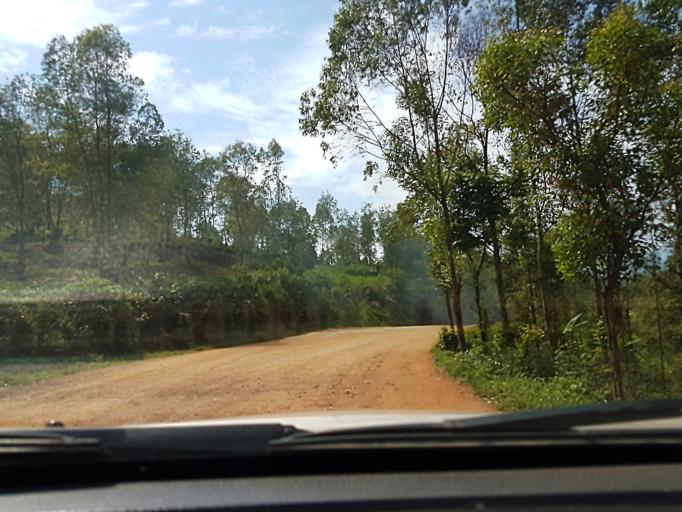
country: CD
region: South Kivu
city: Bukavu
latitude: -2.6312
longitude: 28.8758
